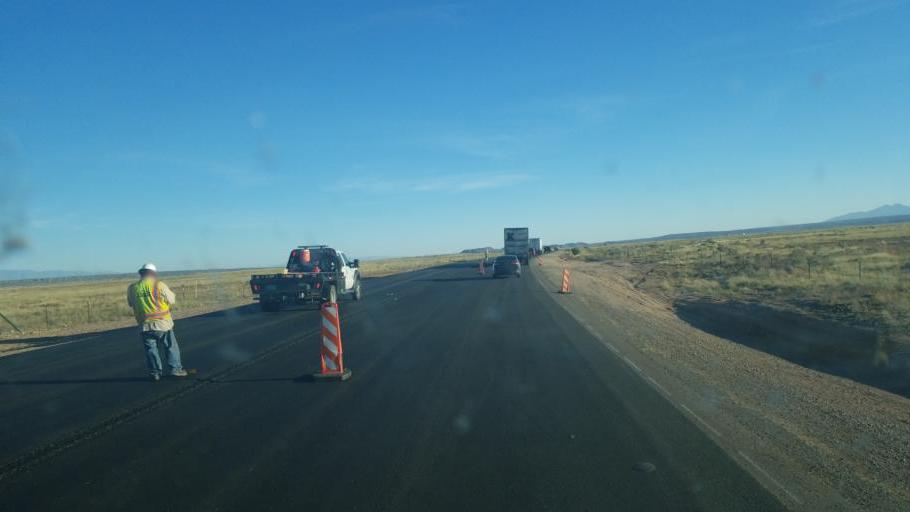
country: US
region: New Mexico
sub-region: Valencia County
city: Los Lunas
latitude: 34.8751
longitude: -107.0557
